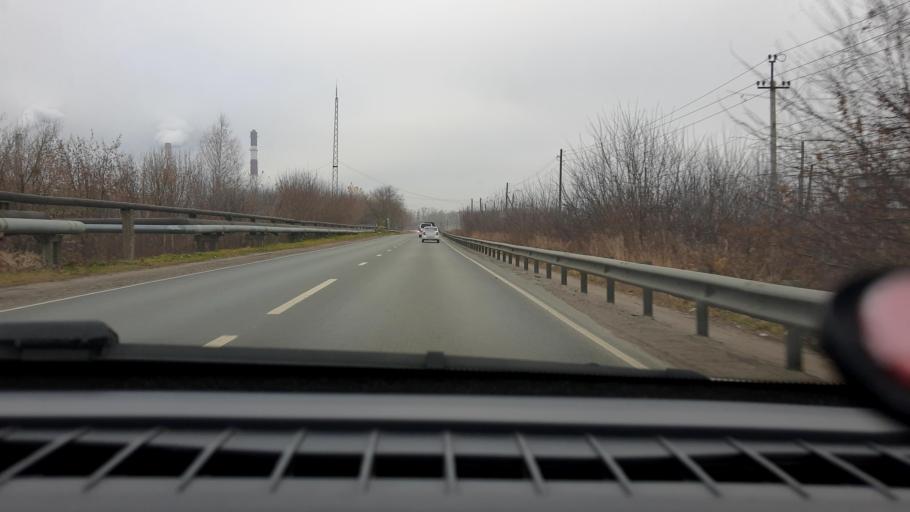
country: RU
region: Nizjnij Novgorod
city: Novaya Balakhna
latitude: 56.4931
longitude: 43.5953
